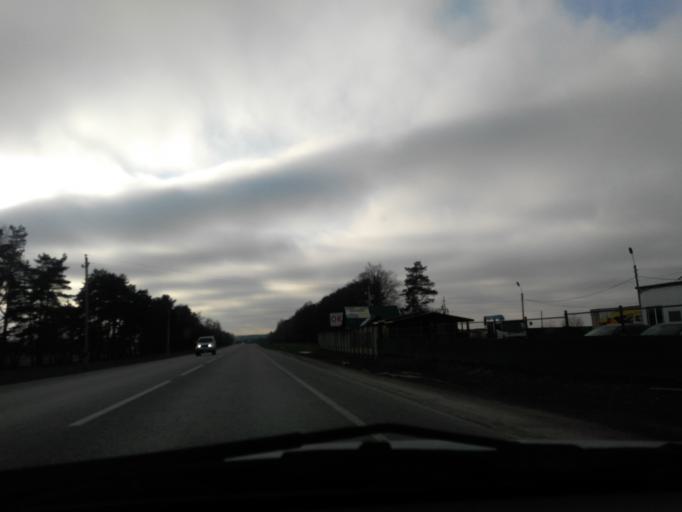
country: RU
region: Moskovskaya
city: Troitsk
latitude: 55.3523
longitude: 37.1836
